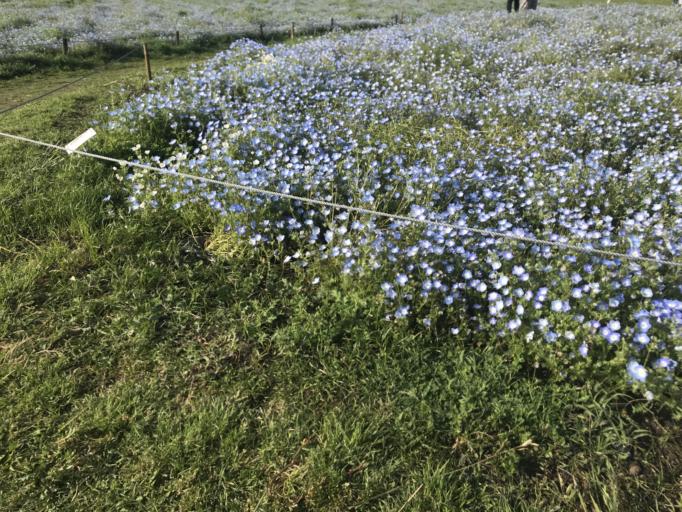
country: JP
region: Fukuoka
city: Fukuoka-shi
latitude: 33.6567
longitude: 130.3497
